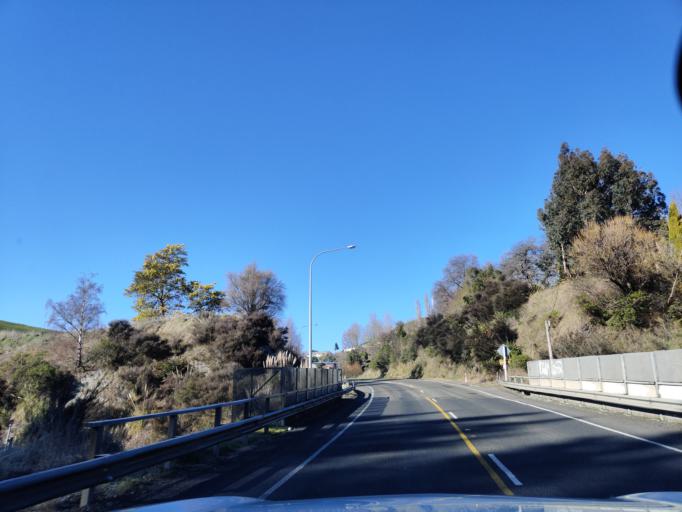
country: NZ
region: Manawatu-Wanganui
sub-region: Ruapehu District
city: Waiouru
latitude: -39.6836
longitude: 175.8011
